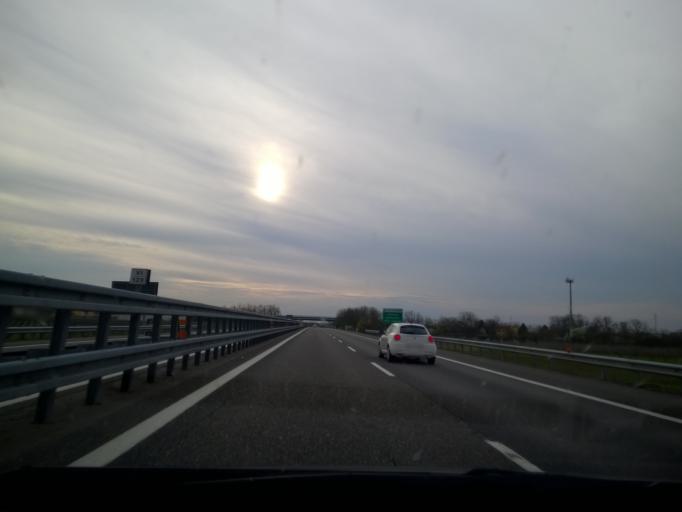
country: IT
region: Lombardy
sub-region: Provincia di Pavia
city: Stradella
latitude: 45.0832
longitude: 9.3075
